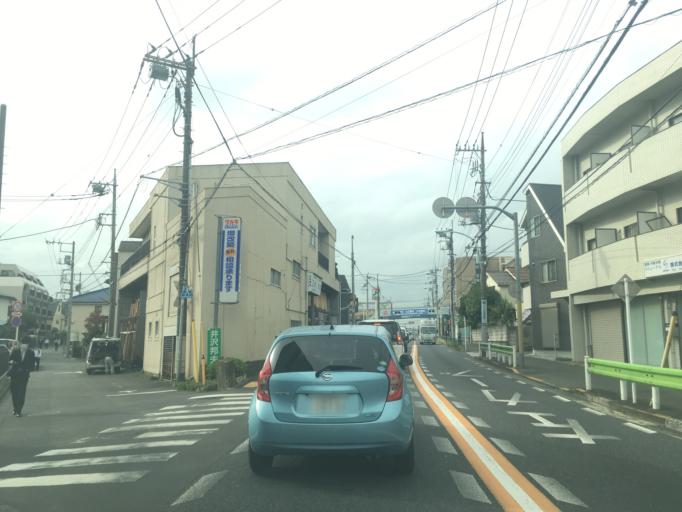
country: JP
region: Tokyo
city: Kokubunji
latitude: 35.7076
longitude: 139.4683
